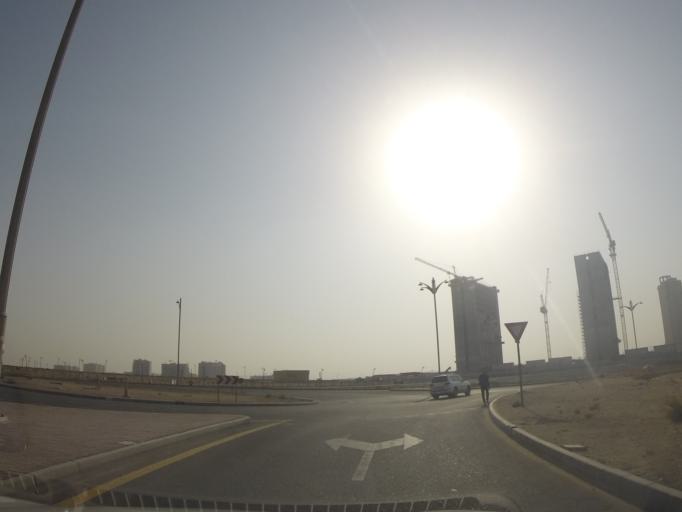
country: AE
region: Dubai
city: Dubai
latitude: 25.0374
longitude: 55.1999
